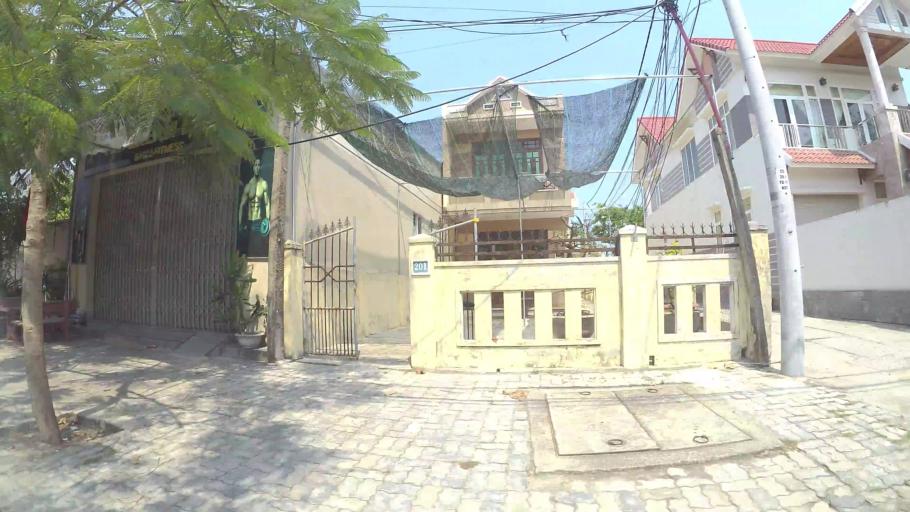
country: VN
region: Da Nang
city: Ngu Hanh Son
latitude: 15.9940
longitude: 108.2651
